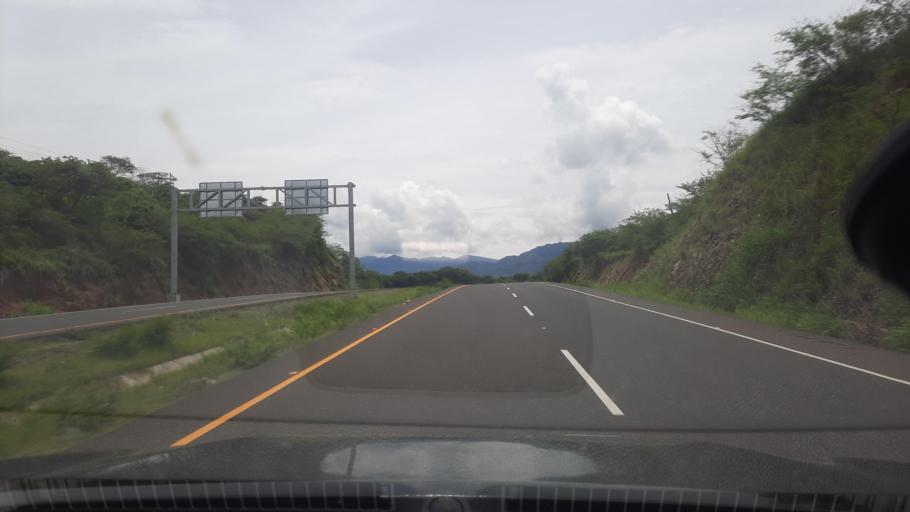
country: HN
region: Valle
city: Aramecina
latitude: 13.6918
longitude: -87.7177
